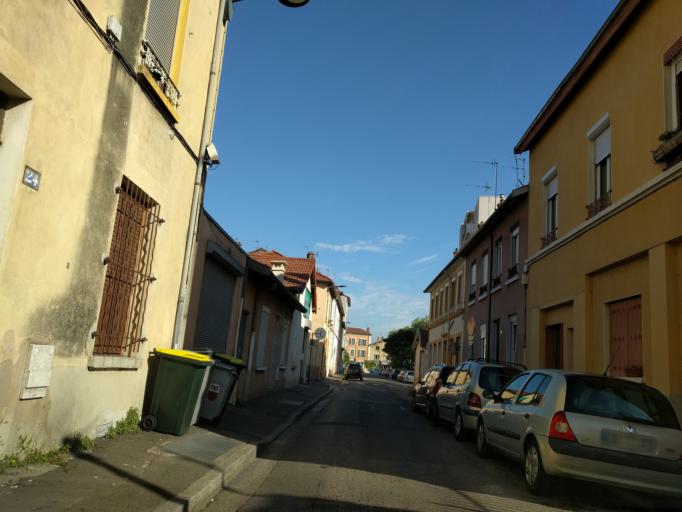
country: FR
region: Rhone-Alpes
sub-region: Departement du Rhone
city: Villeurbanne
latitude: 45.7646
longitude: 4.8985
